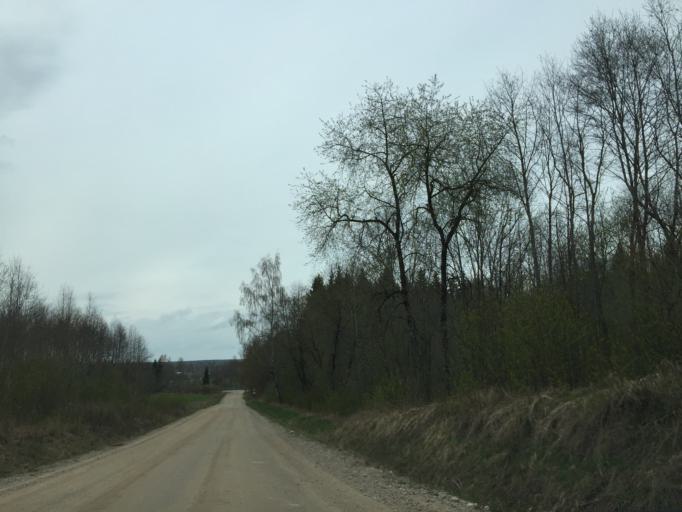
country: LV
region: Priekuli
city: Priekuli
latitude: 57.3438
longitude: 25.3482
